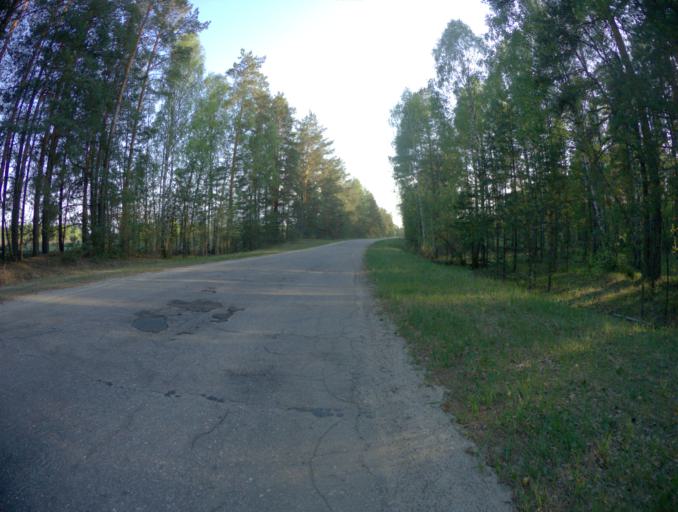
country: RU
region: Vladimir
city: Vyazniki
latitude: 56.3417
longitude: 42.1393
